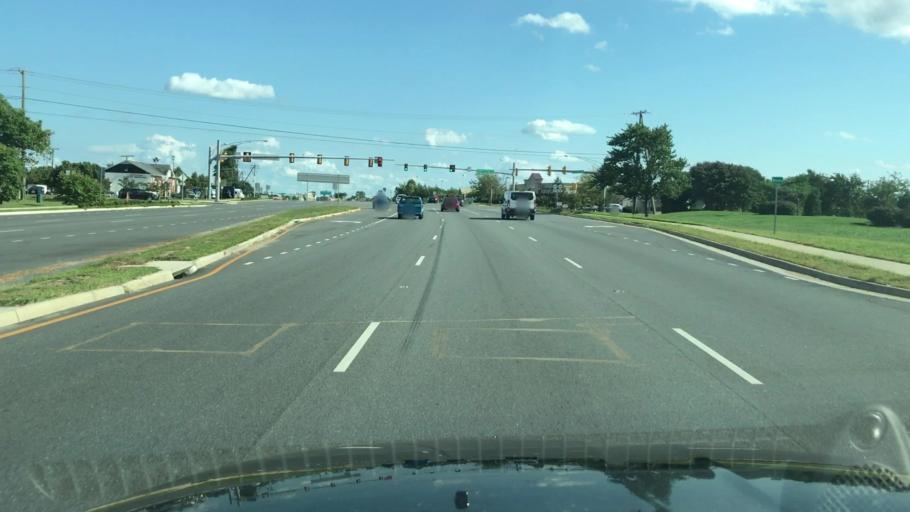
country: US
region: Virginia
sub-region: Stafford County
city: Falmouth
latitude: 38.3625
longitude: -77.5211
